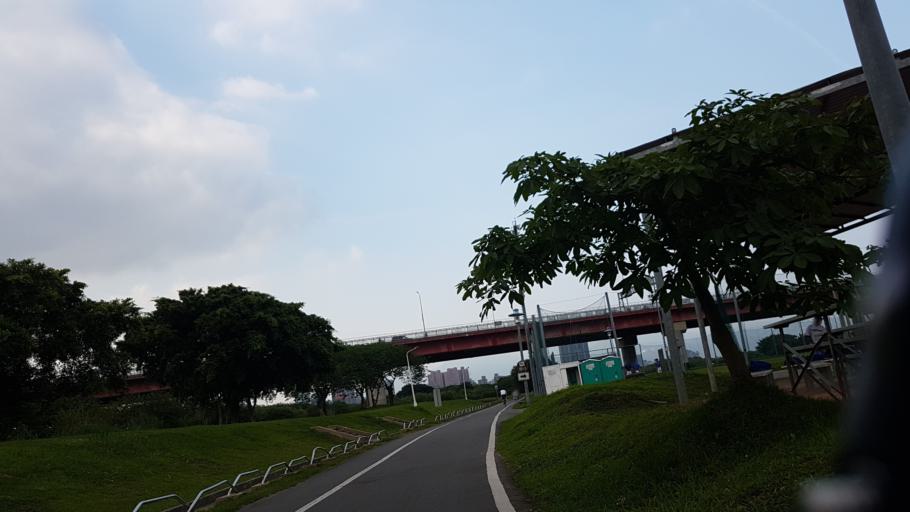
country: TW
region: Taipei
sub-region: Taipei
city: Banqiao
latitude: 25.0344
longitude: 121.4864
